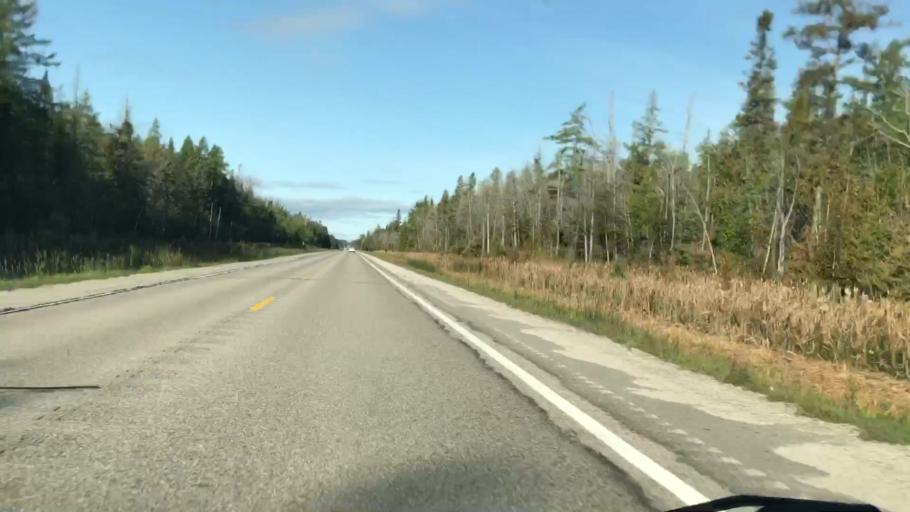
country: US
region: Michigan
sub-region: Luce County
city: Newberry
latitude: 46.3037
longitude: -85.3017
